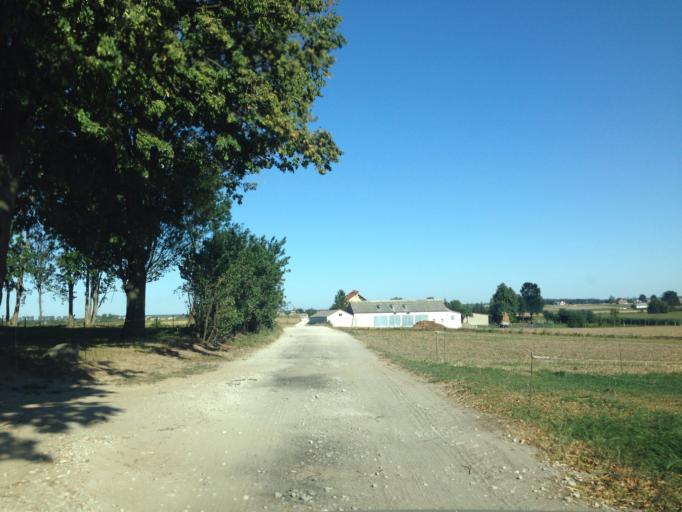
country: PL
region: Kujawsko-Pomorskie
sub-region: Powiat brodnicki
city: Swiedziebnia
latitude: 53.1898
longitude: 19.5736
